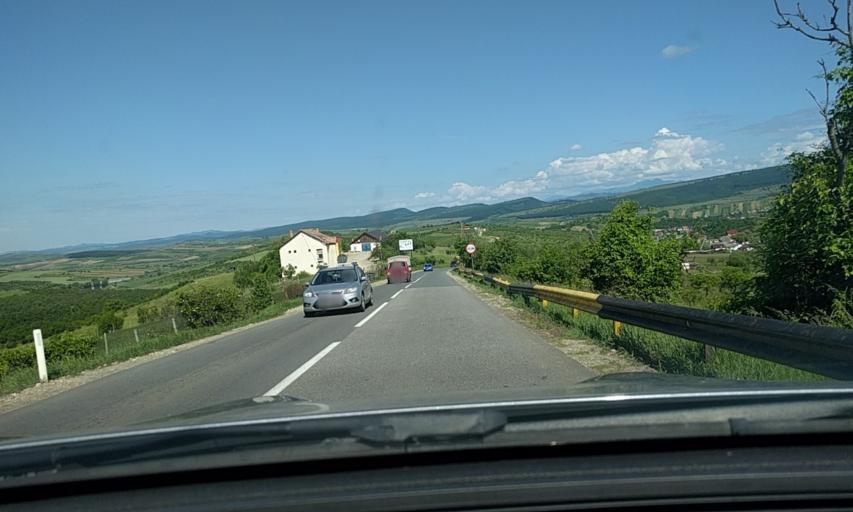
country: RO
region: Bistrita-Nasaud
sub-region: Comuna Dumitra
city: Dumitra
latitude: 47.2030
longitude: 24.4757
